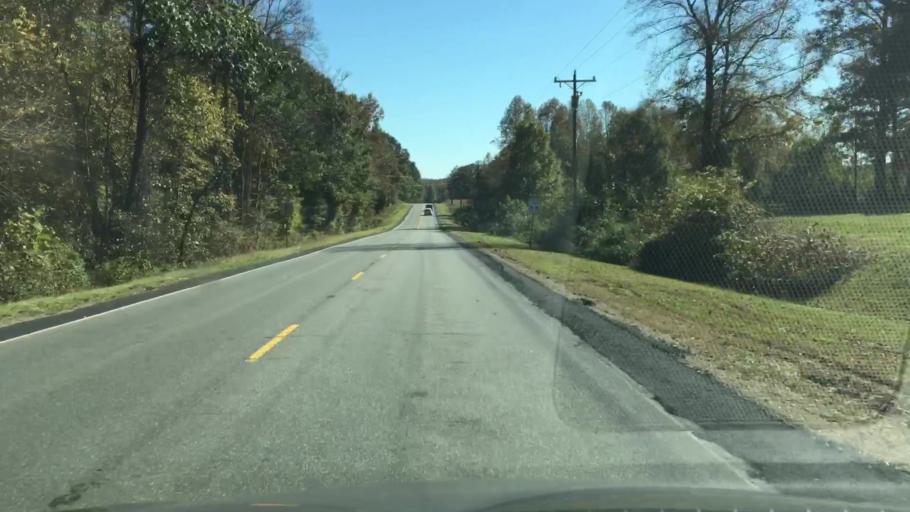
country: US
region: North Carolina
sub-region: Rockingham County
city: Reidsville
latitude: 36.2863
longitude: -79.6552
